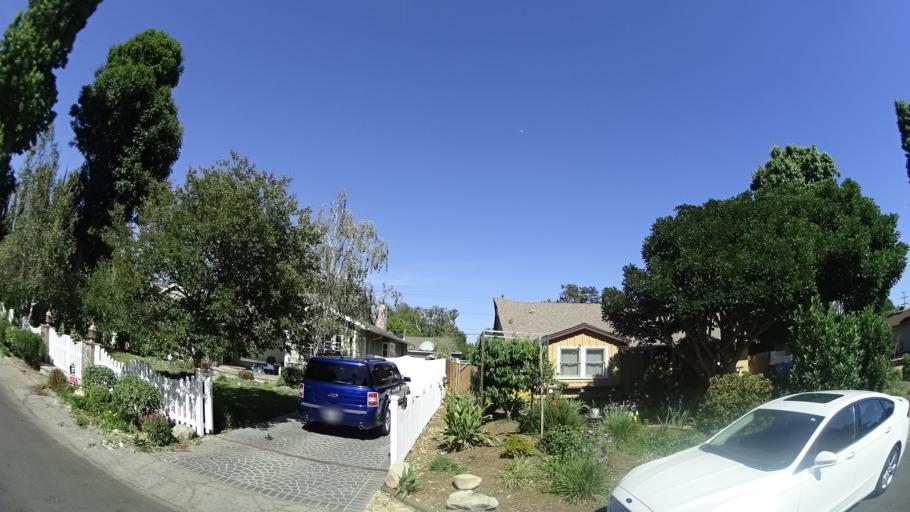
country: US
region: California
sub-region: Los Angeles County
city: Van Nuys
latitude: 34.1712
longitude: -118.4280
